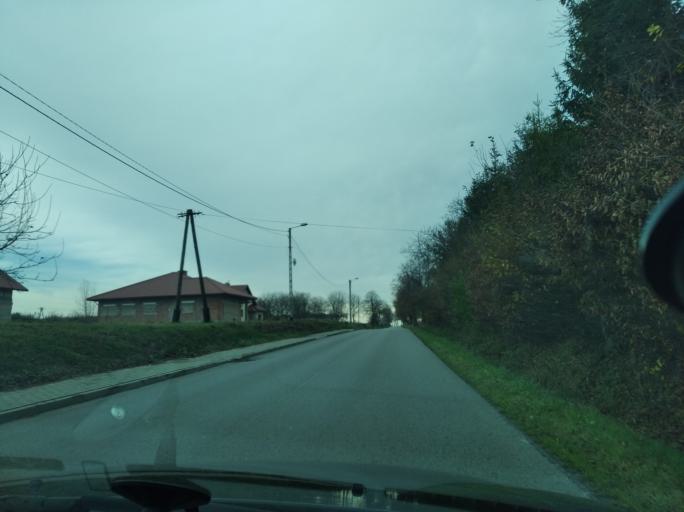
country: PL
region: Subcarpathian Voivodeship
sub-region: Powiat lancucki
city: Albigowa
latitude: 50.0314
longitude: 22.2394
